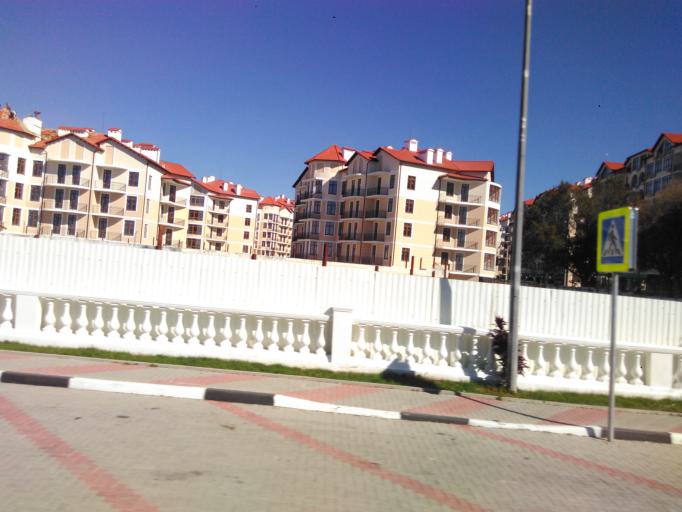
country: RU
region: Krasnodarskiy
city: Gelendzhik
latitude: 44.5473
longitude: 38.0579
